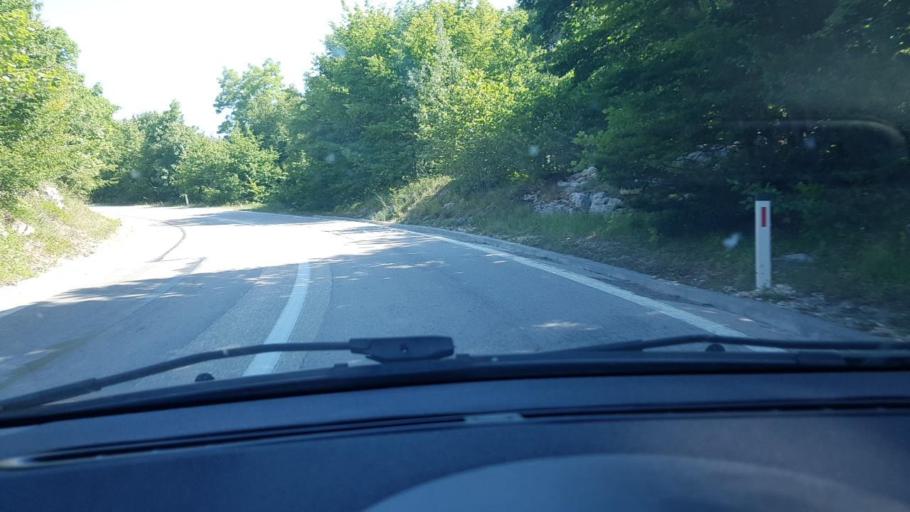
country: BA
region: Federation of Bosnia and Herzegovina
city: Bosansko Grahovo
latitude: 44.3113
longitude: 16.3120
